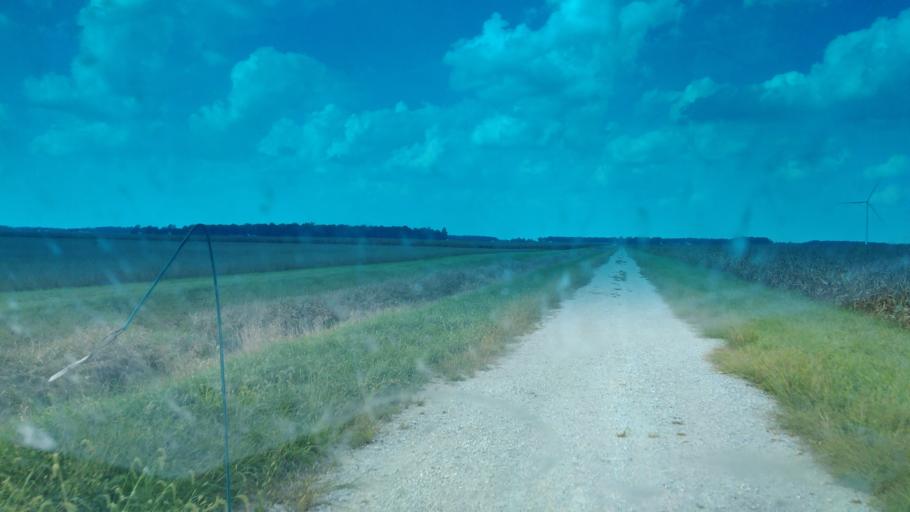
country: US
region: Ohio
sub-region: Hancock County
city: Arlington
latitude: 40.7908
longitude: -83.6900
